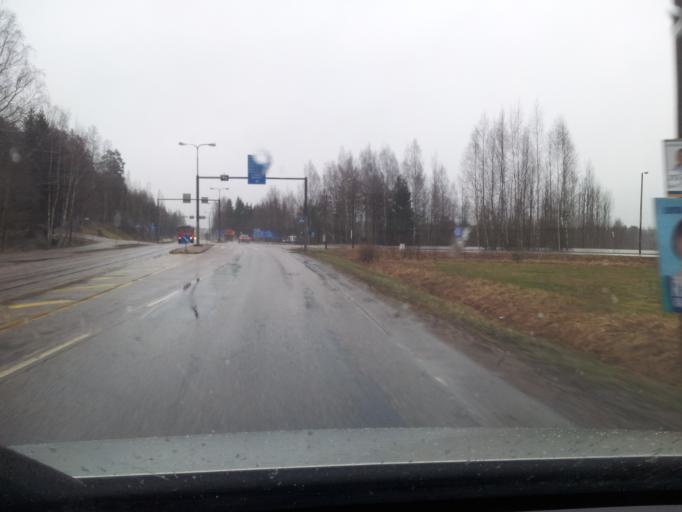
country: FI
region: Uusimaa
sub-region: Helsinki
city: Espoo
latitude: 60.1909
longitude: 24.5721
